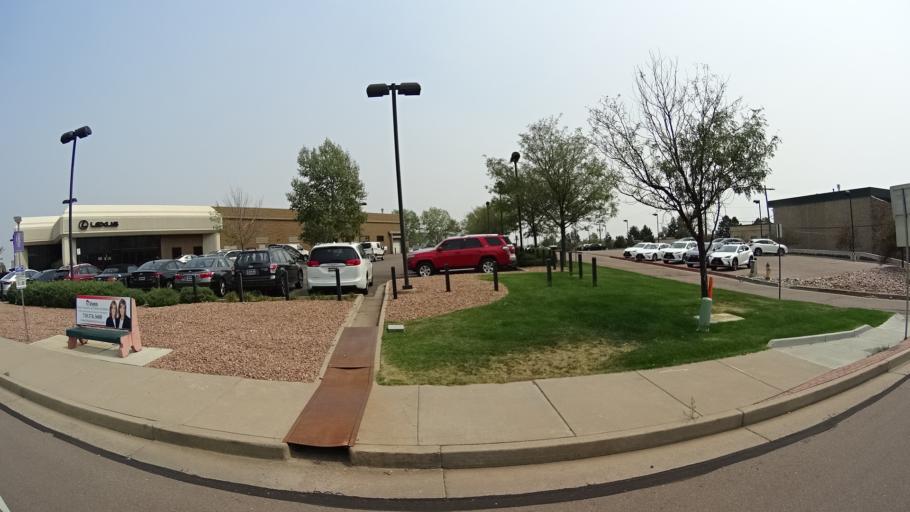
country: US
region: Colorado
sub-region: El Paso County
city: Colorado Springs
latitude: 38.8150
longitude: -104.8409
